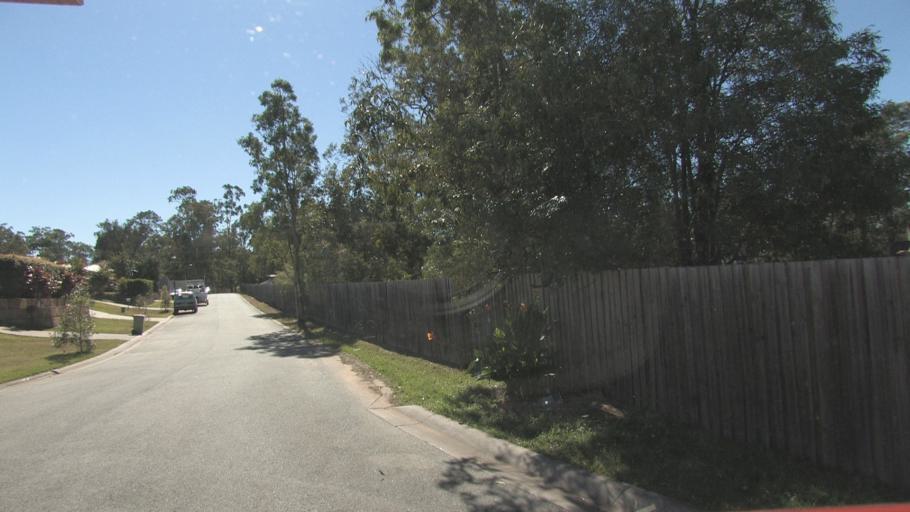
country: AU
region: Queensland
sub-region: Logan
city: Park Ridge South
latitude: -27.6715
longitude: 153.0244
